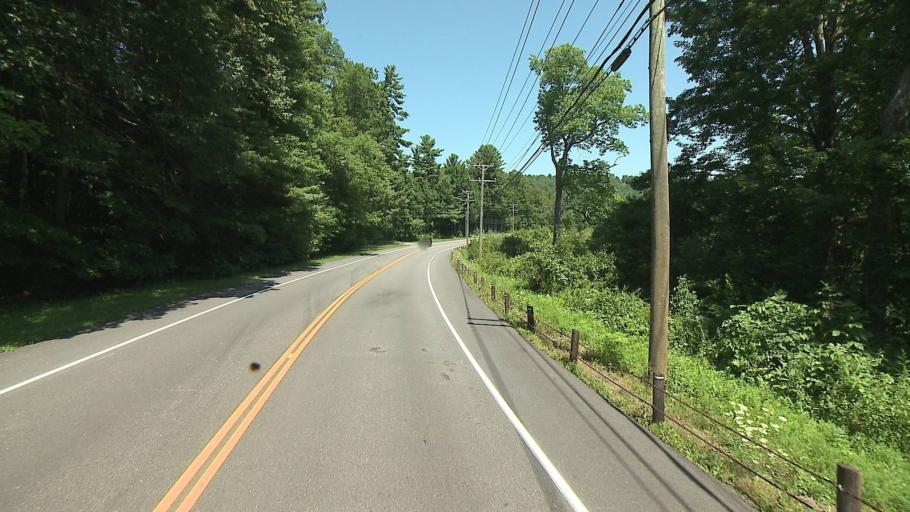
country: US
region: Connecticut
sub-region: Litchfield County
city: New Preston
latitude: 41.8382
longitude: -73.3498
